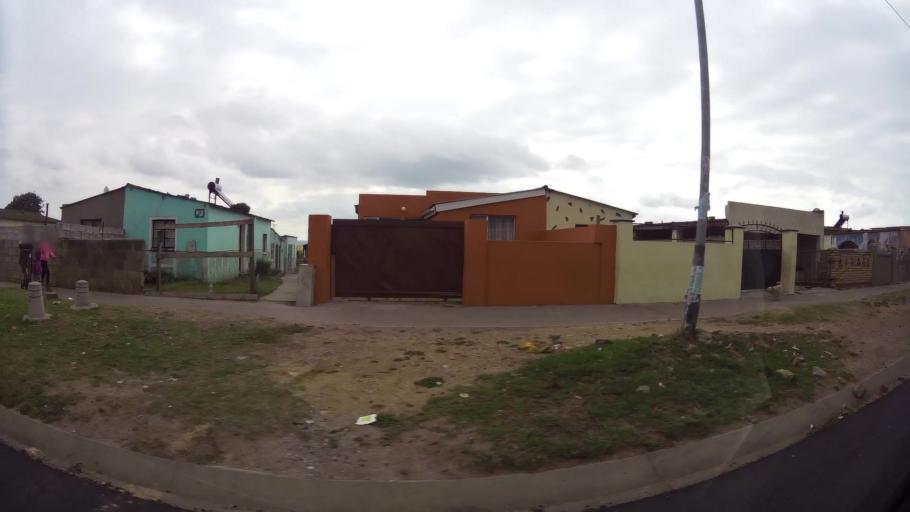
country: ZA
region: Eastern Cape
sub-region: Nelson Mandela Bay Metropolitan Municipality
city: Port Elizabeth
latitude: -33.8916
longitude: 25.5939
